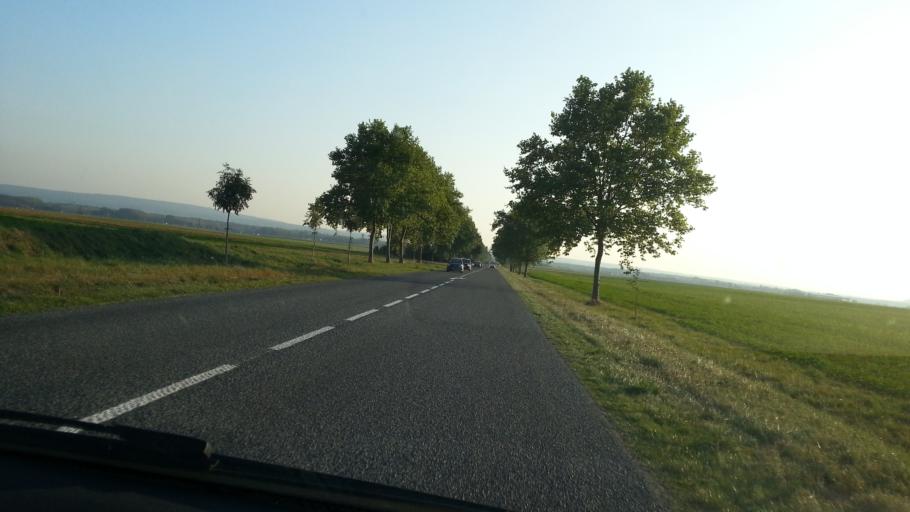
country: FR
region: Picardie
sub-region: Departement de l'Oise
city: Saint-Martin-Longueau
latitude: 49.3647
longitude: 2.6137
